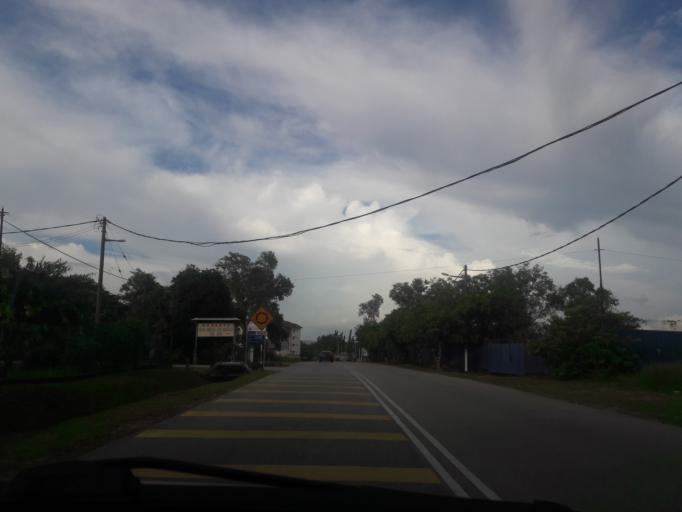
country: MY
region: Kedah
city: Sungai Petani
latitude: 5.6519
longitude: 100.4870
